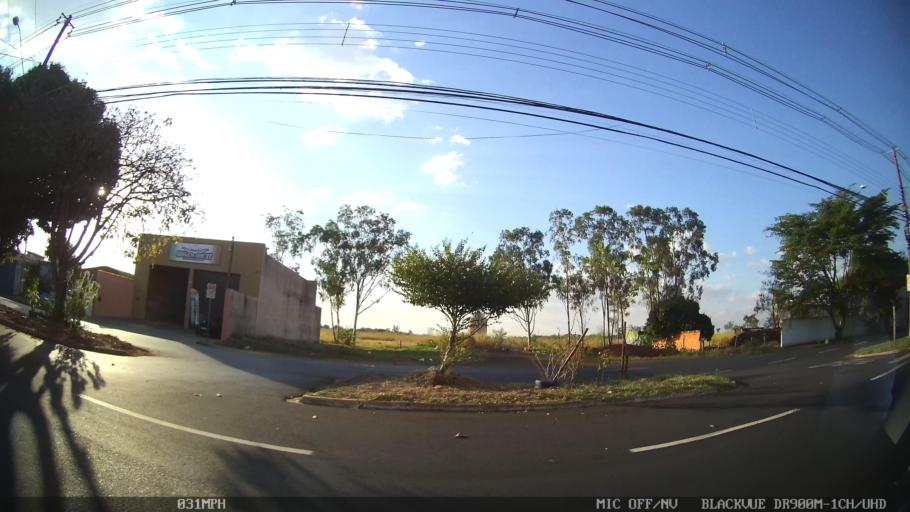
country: BR
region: Sao Paulo
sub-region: Ribeirao Preto
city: Ribeirao Preto
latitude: -21.1676
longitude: -47.7511
